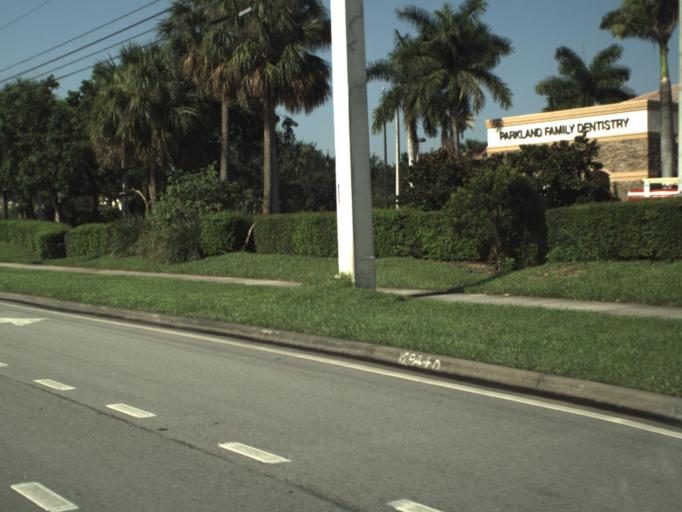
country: US
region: Florida
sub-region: Broward County
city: Parkland
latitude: 26.3240
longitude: -80.2029
